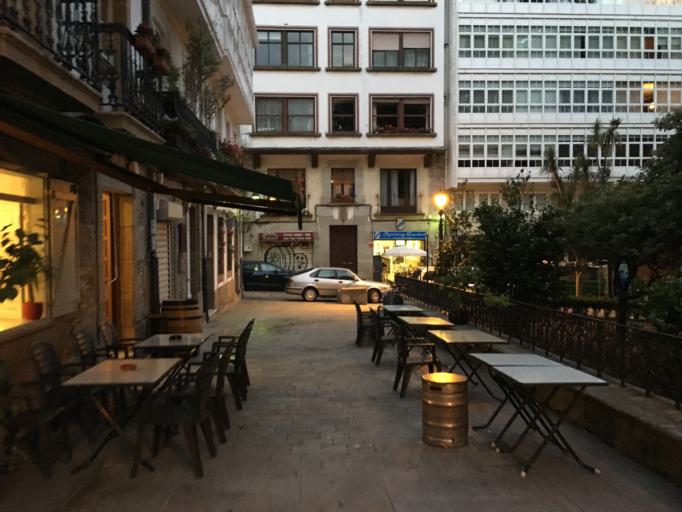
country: ES
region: Galicia
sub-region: Provincia da Coruna
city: A Coruna
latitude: 43.3701
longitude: -8.3933
